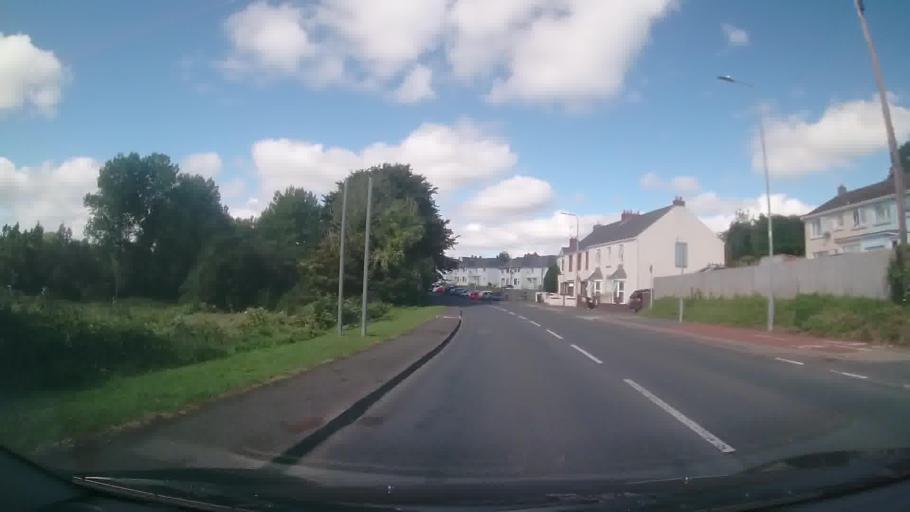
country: GB
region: Wales
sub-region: Pembrokeshire
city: Tenby
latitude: 51.6723
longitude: -4.7154
